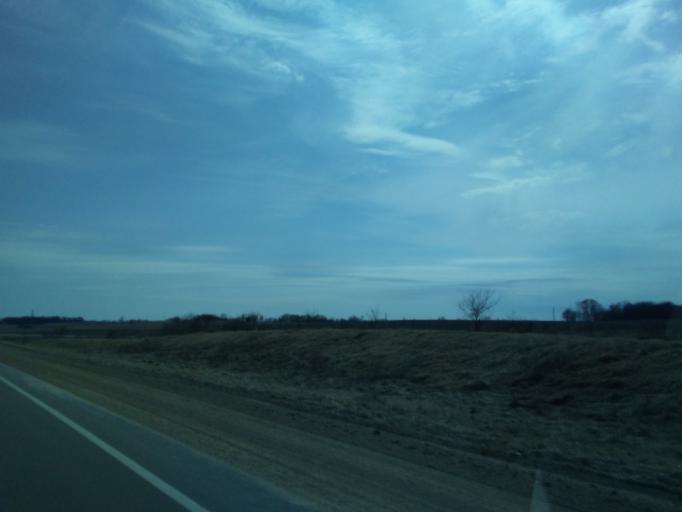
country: US
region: Iowa
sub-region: Winneshiek County
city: Decorah
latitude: 43.4126
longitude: -91.8582
